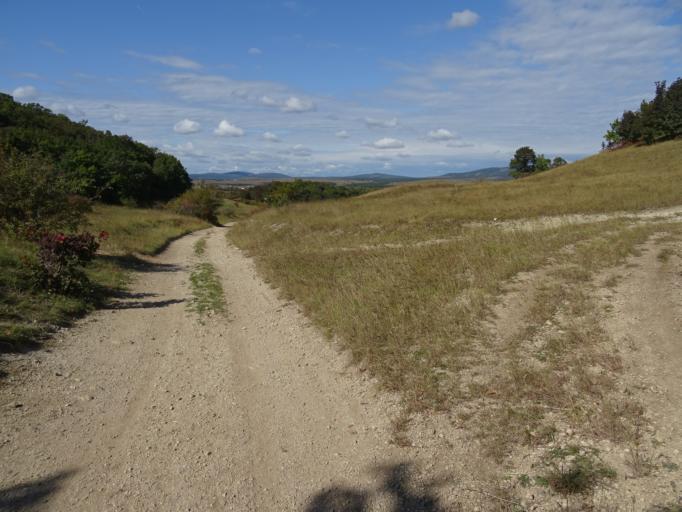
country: HU
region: Veszprem
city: Petfuerdo
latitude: 47.1601
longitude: 18.1020
